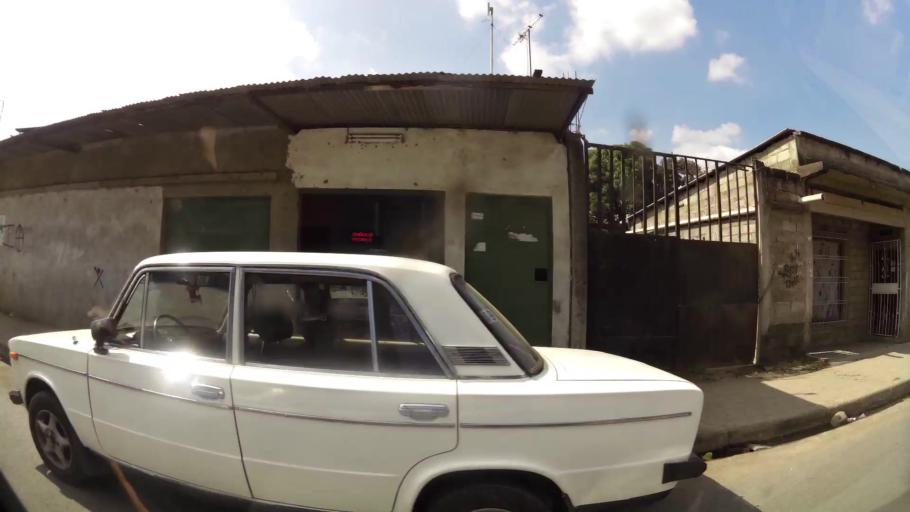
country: EC
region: Guayas
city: Eloy Alfaro
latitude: -2.1694
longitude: -79.8263
